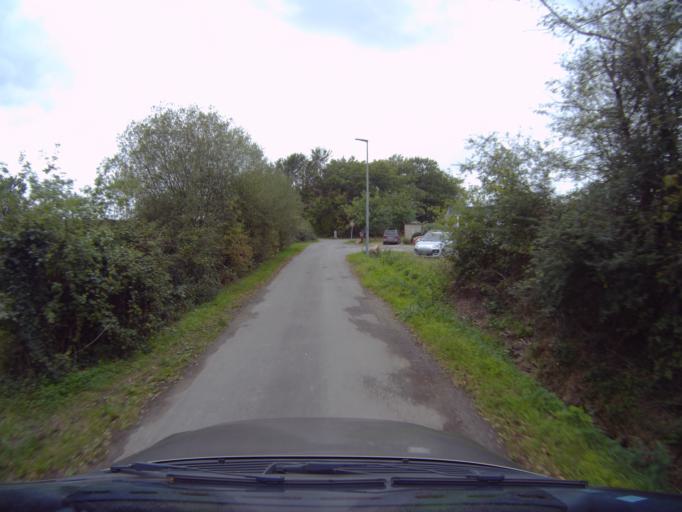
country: FR
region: Pays de la Loire
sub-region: Departement de la Loire-Atlantique
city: Clisson
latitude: 47.1046
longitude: -1.2664
